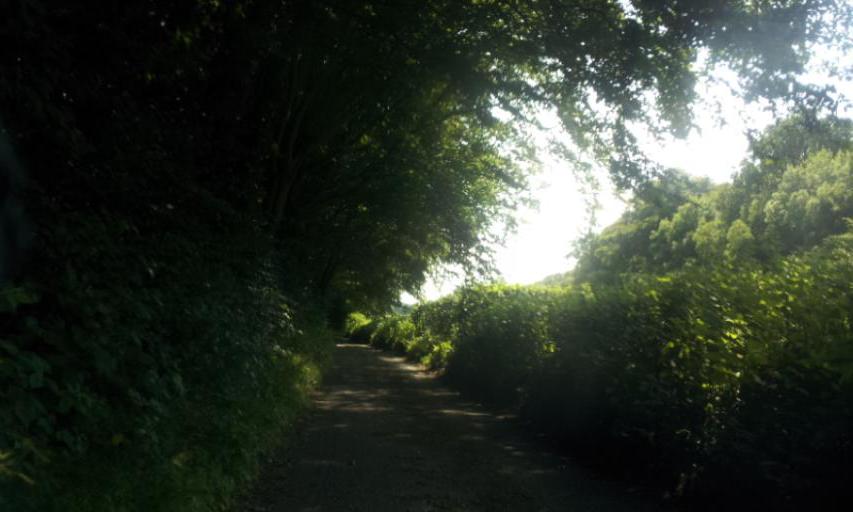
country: GB
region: England
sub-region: Kent
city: Lenham
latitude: 51.2771
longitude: 0.7649
